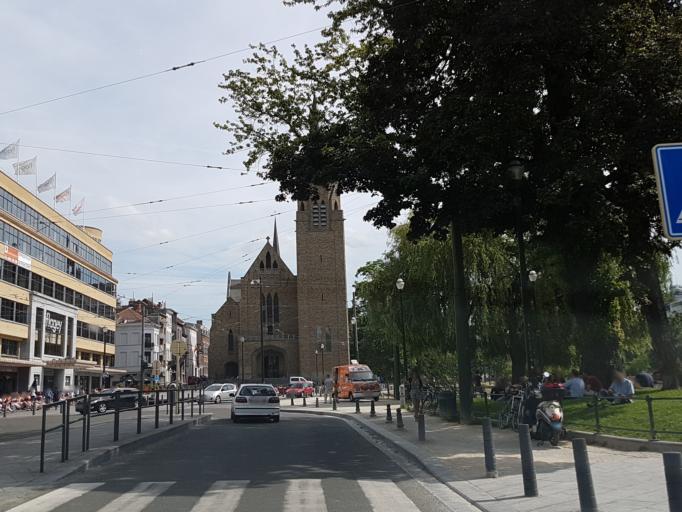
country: BE
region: Brussels Capital
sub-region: Bruxelles-Capitale
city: Brussels
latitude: 50.8274
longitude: 4.3718
